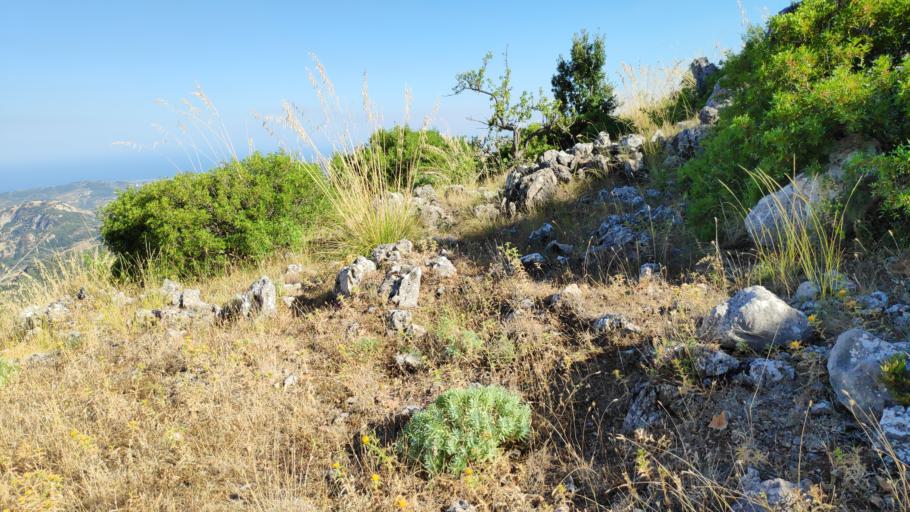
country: IT
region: Calabria
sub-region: Provincia di Reggio Calabria
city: Pazzano
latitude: 38.4622
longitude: 16.4419
